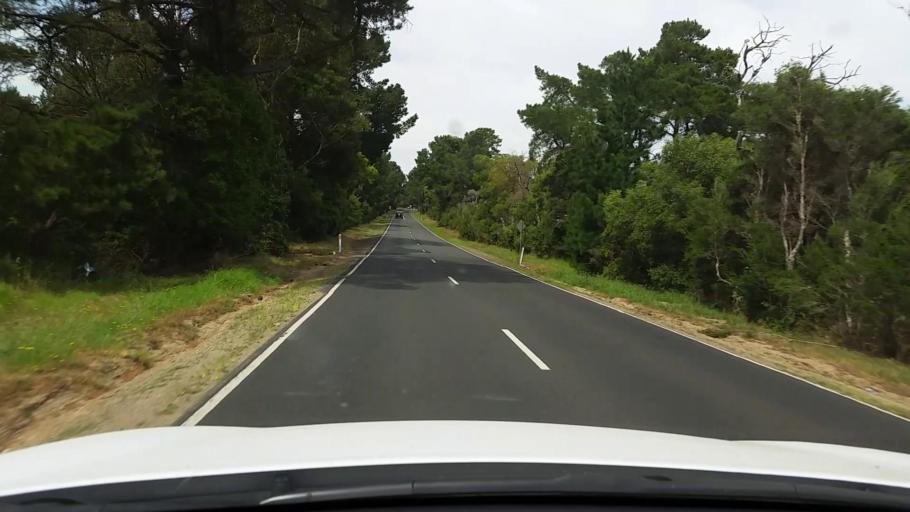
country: AU
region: Victoria
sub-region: Mornington Peninsula
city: Balnarring
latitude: -38.3778
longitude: 145.1112
